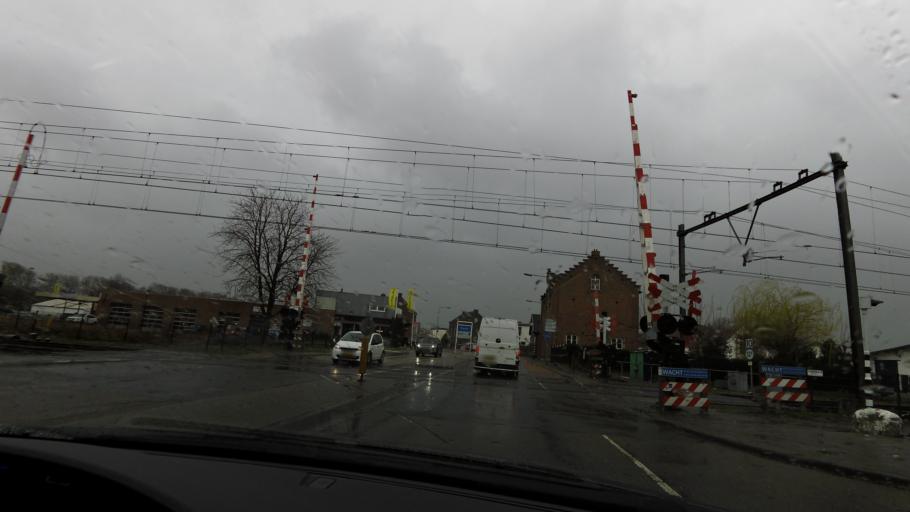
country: NL
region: Limburg
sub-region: Gemeente Stein
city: Elsloo
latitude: 50.9464
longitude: 5.7836
